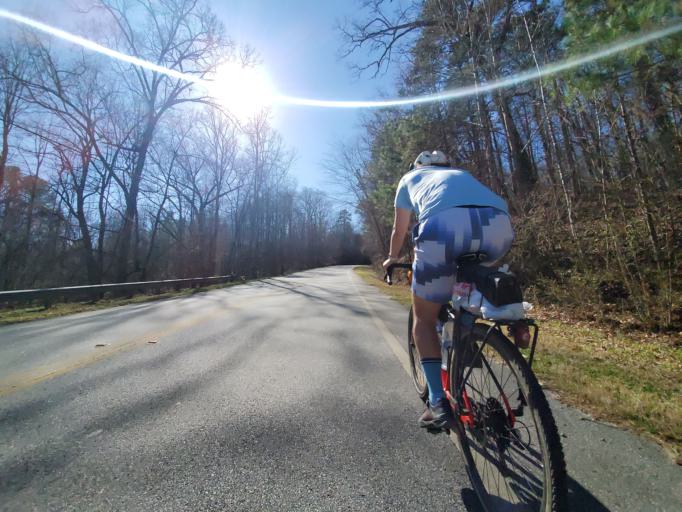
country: US
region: Georgia
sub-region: Gwinnett County
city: Dacula
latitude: 33.9622
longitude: -83.9277
